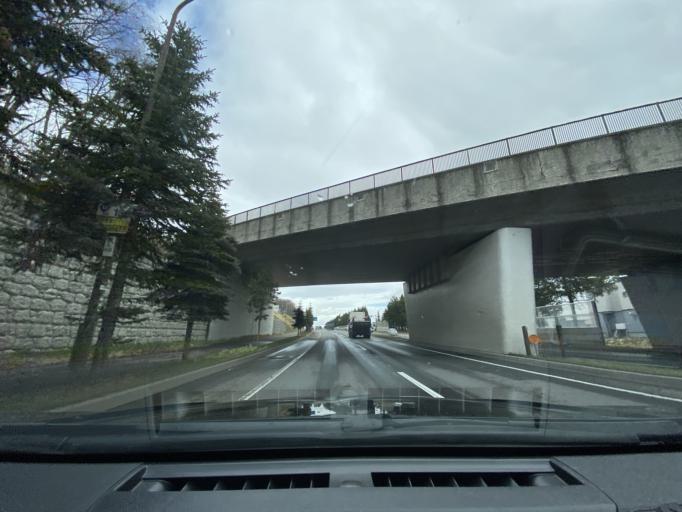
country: JP
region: Hokkaido
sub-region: Asahikawa-shi
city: Asahikawa
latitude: 43.8129
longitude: 142.3670
